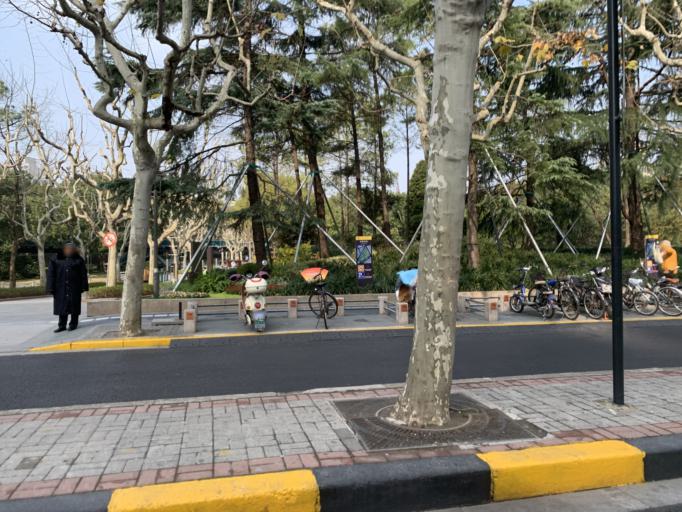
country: CN
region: Shanghai Shi
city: Xuhui
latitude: 31.1985
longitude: 121.4383
